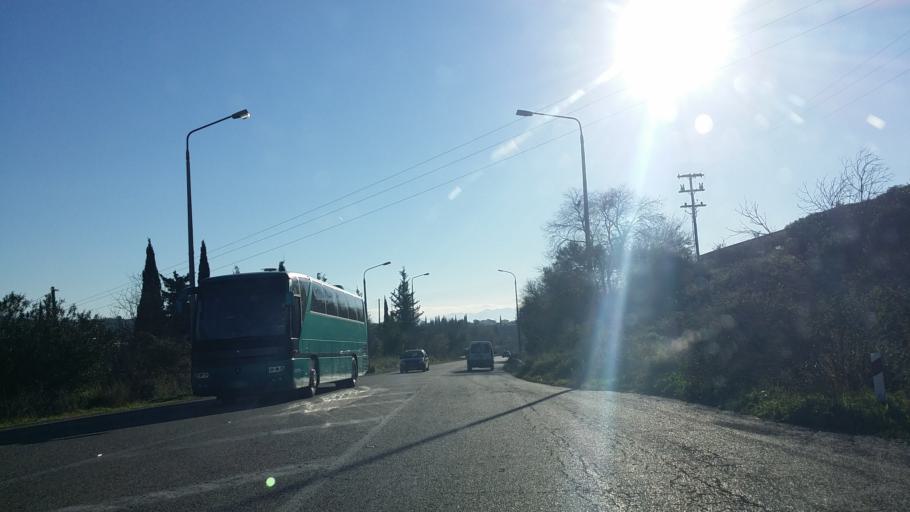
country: GR
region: West Greece
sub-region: Nomos Aitolias kai Akarnanias
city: Fitiai
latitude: 38.6972
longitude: 21.2191
